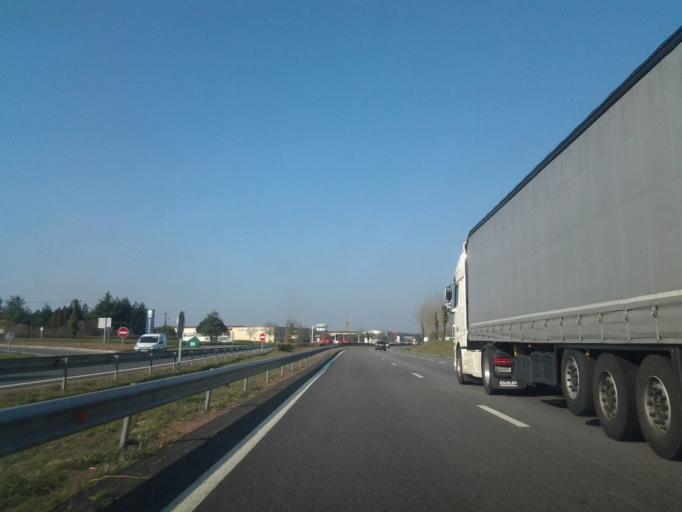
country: FR
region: Pays de la Loire
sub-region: Departement de la Vendee
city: La Genetouze
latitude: 46.7245
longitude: -1.5608
